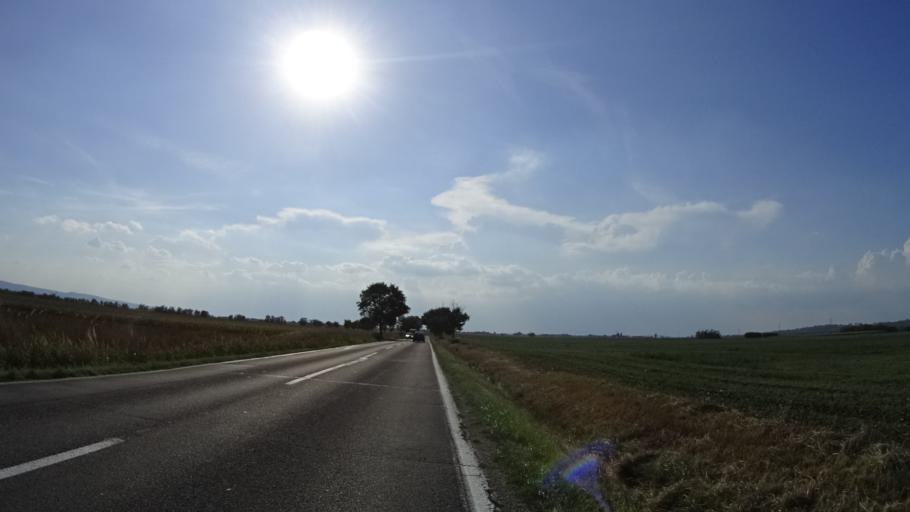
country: HU
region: Komarom-Esztergom
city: Tat
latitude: 47.7911
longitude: 18.6353
